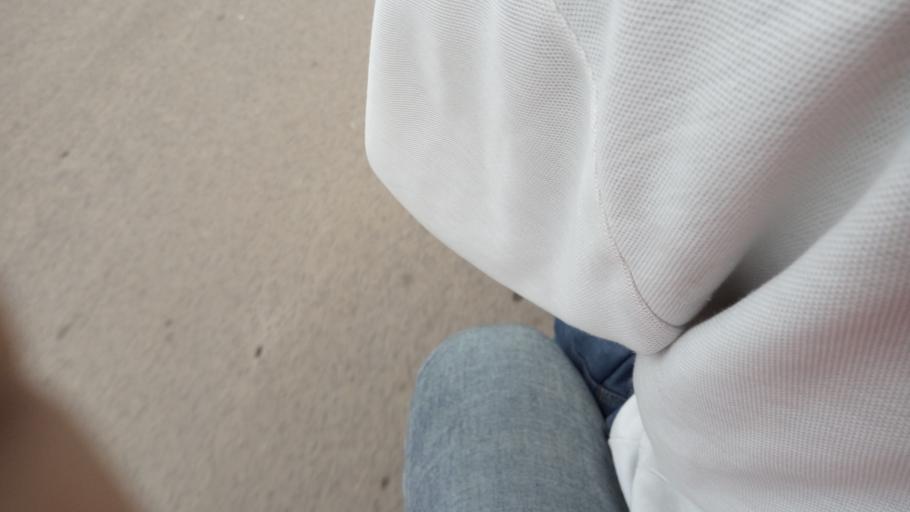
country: CD
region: Kinshasa
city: Masina
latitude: -4.4067
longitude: 15.3163
